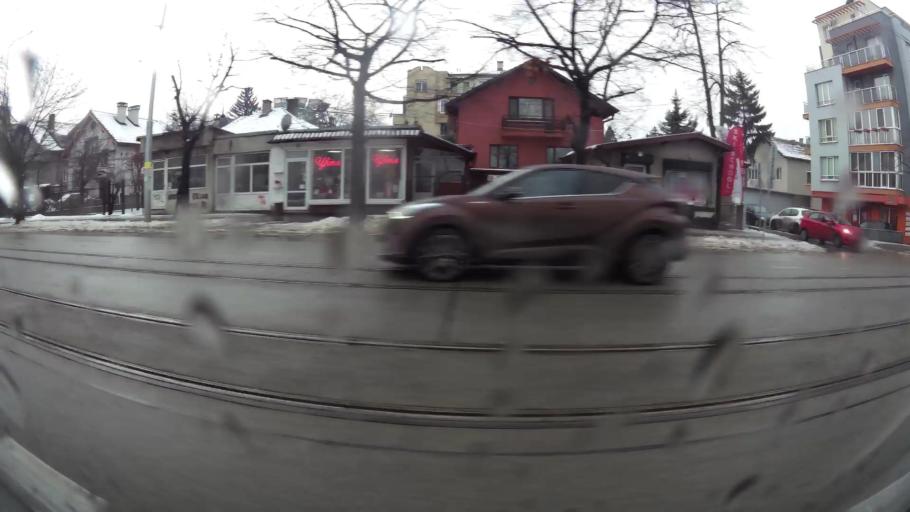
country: BG
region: Sofia-Capital
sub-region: Stolichna Obshtina
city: Sofia
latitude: 42.6736
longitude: 23.2700
